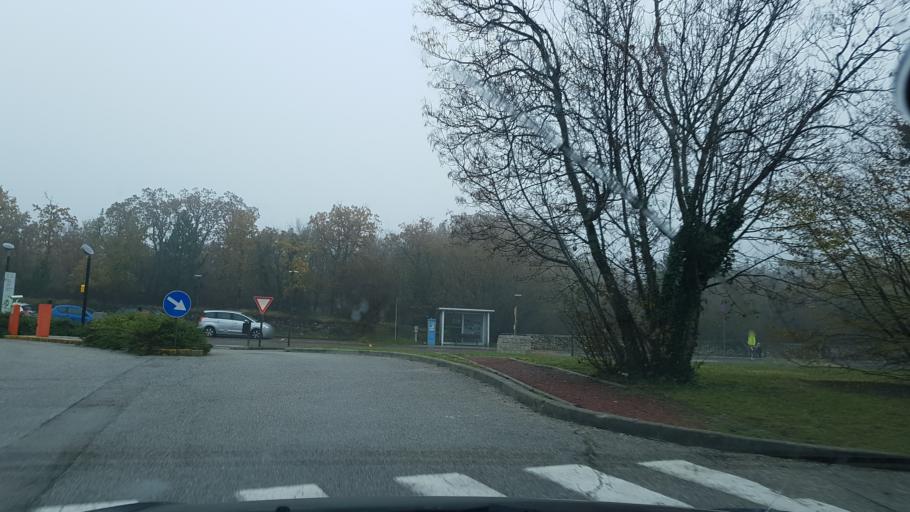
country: IT
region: Friuli Venezia Giulia
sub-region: Provincia di Trieste
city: Domio
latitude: 45.6443
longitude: 13.8479
